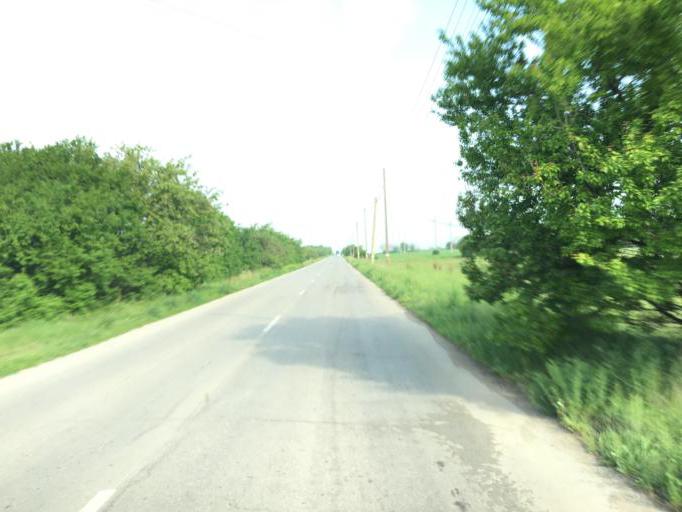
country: BG
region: Kyustendil
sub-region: Obshtina Bobovdol
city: Bobovdol
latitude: 42.4791
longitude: 23.0617
